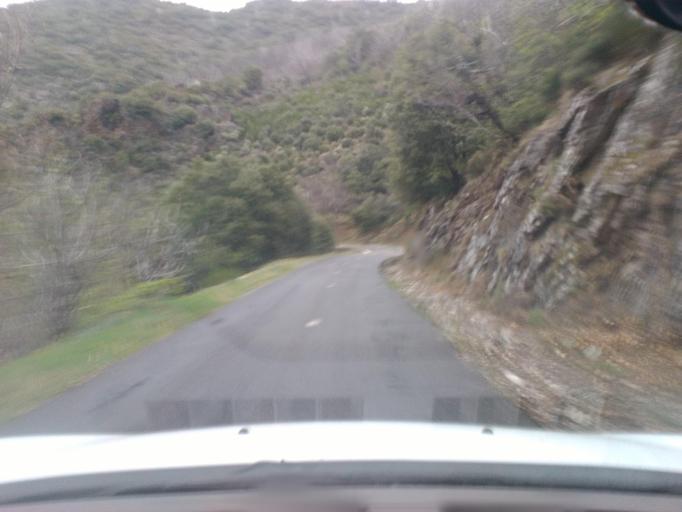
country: FR
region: Languedoc-Roussillon
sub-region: Departement du Gard
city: Valleraugue
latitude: 44.1000
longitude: 3.6435
